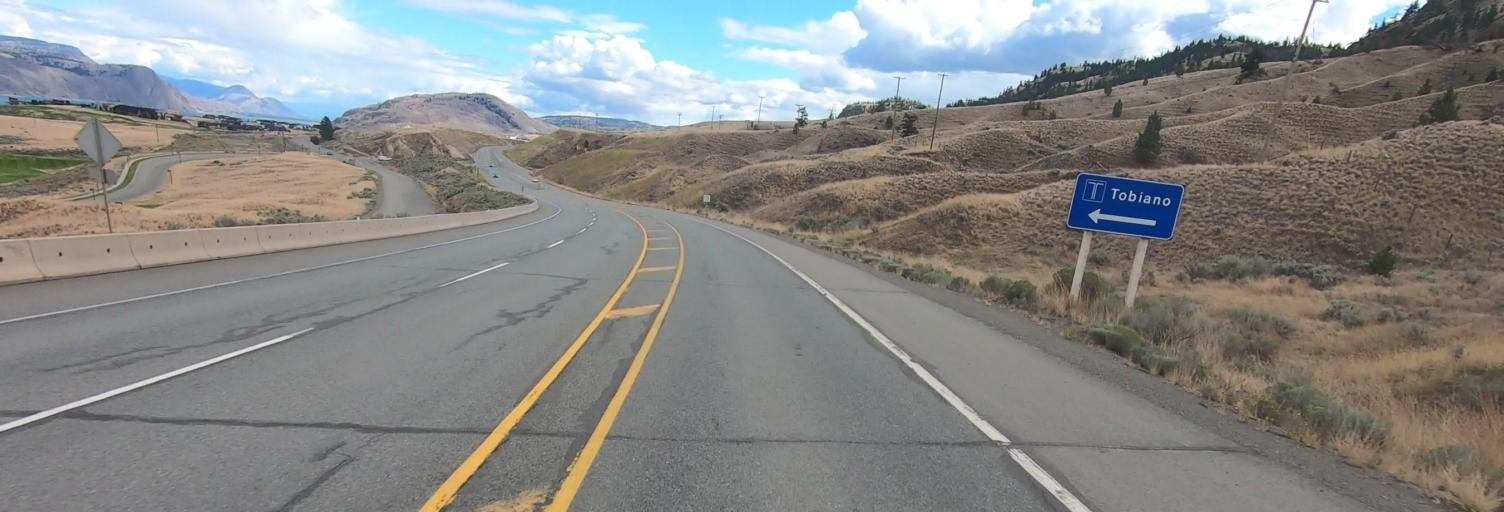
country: CA
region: British Columbia
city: Logan Lake
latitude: 50.7341
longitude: -120.6992
